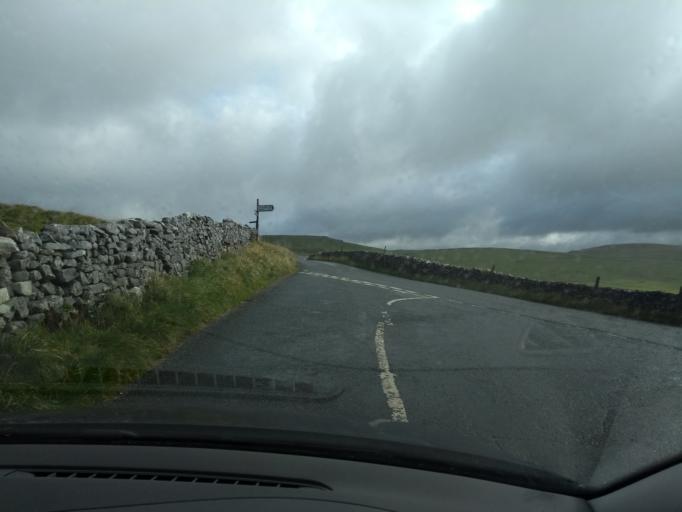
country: GB
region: England
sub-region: North Yorkshire
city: Settle
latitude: 54.1011
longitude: -2.2205
